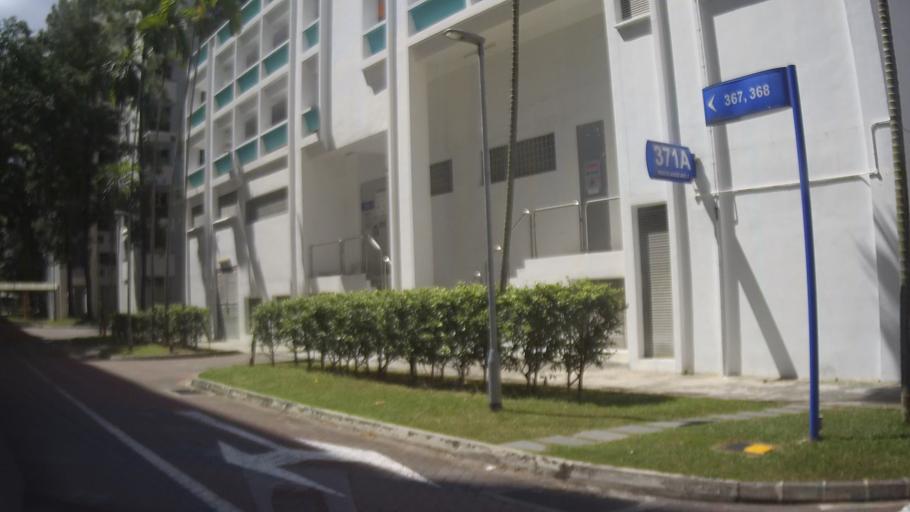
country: MY
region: Johor
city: Johor Bahru
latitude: 1.4334
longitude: 103.7861
